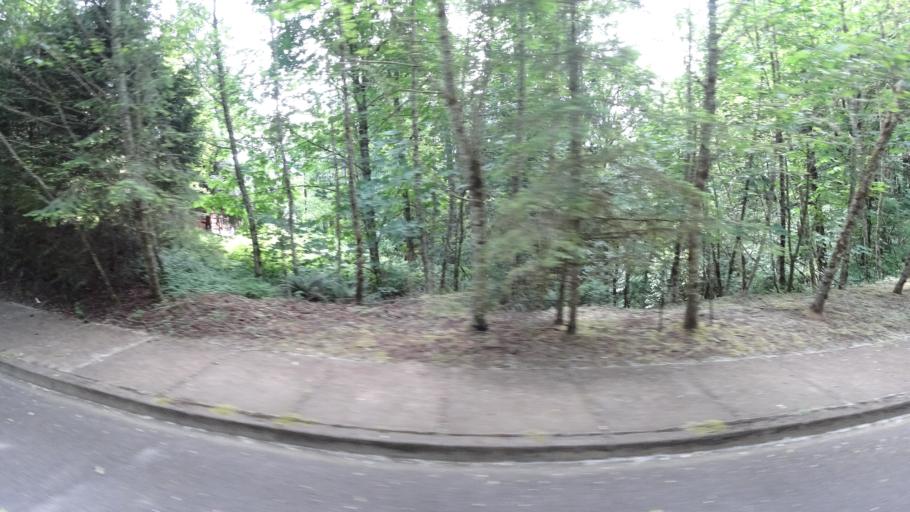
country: US
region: Oregon
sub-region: Washington County
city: Oak Hills
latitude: 45.5947
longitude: -122.8215
